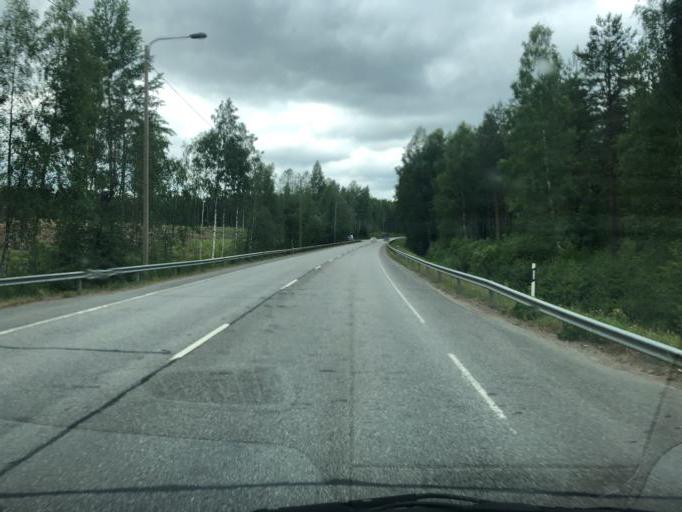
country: FI
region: Kymenlaakso
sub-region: Kouvola
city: Kouvola
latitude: 60.8973
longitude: 26.7483
